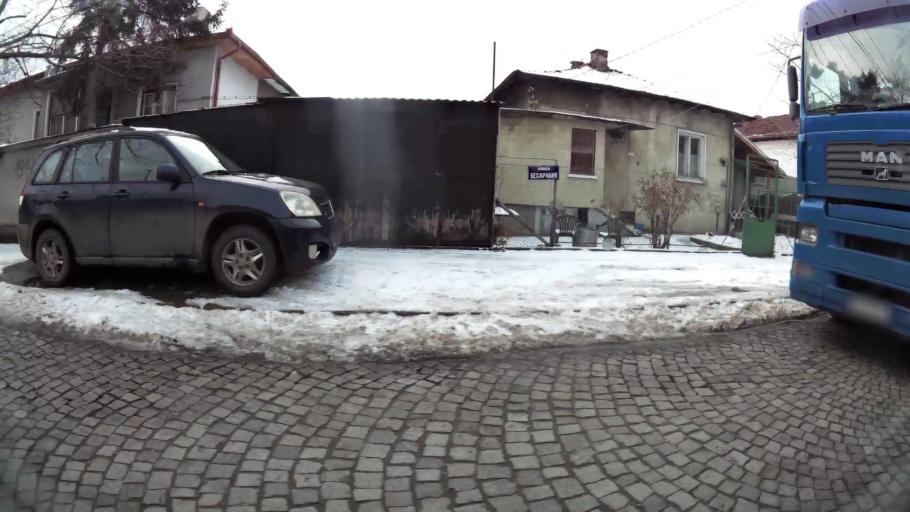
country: BG
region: Sofia-Capital
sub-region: Stolichna Obshtina
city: Sofia
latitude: 42.7061
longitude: 23.3737
